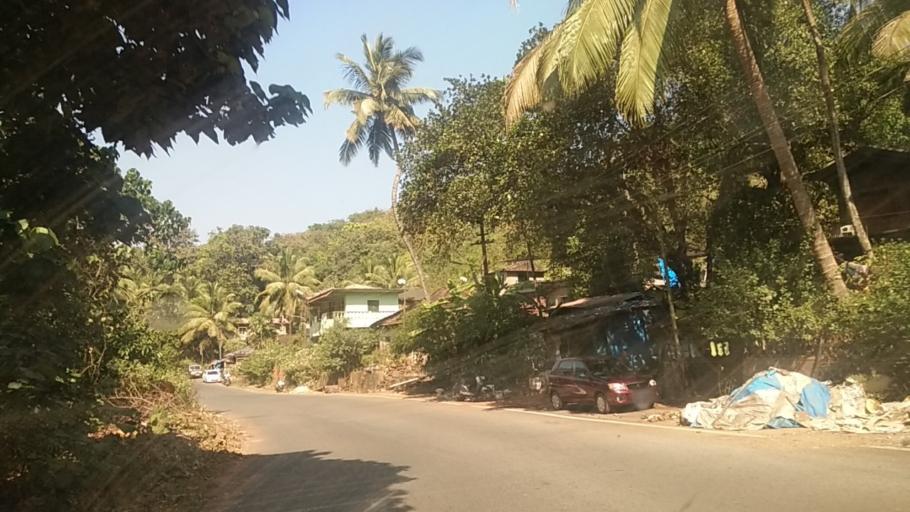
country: IN
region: Goa
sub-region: South Goa
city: Davorlim
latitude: 15.3120
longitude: 74.0380
